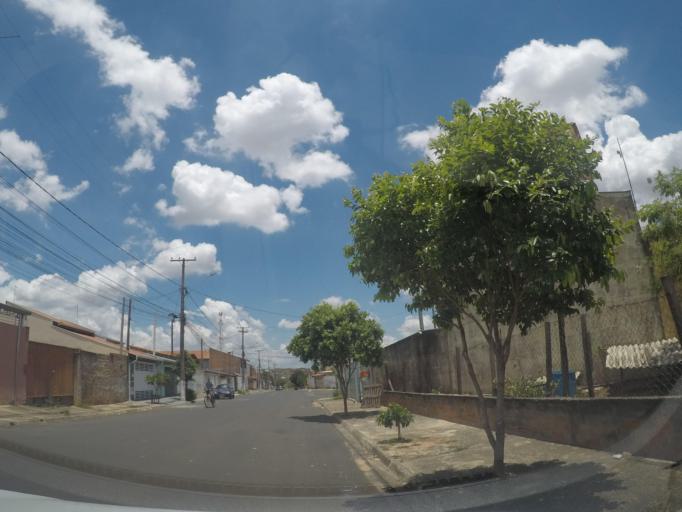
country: BR
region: Sao Paulo
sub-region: Hortolandia
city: Hortolandia
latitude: -22.8416
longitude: -47.2238
